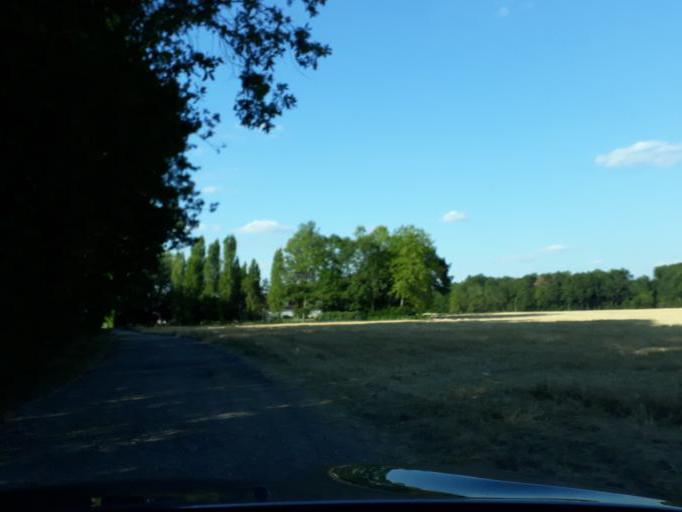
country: FR
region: Centre
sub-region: Departement du Loiret
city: Saint-Ay
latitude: 47.8825
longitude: 1.7351
